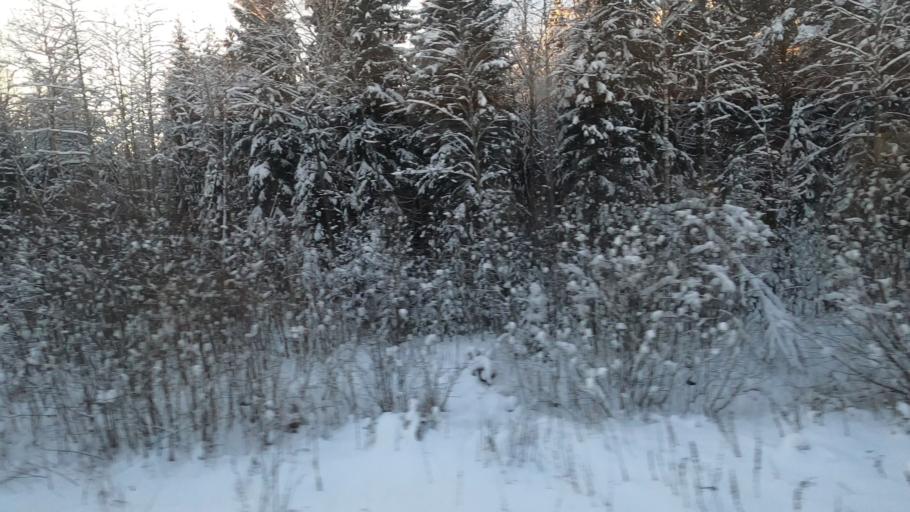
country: RU
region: Moskovskaya
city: Novo-Nikol'skoye
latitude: 56.6142
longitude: 37.5668
